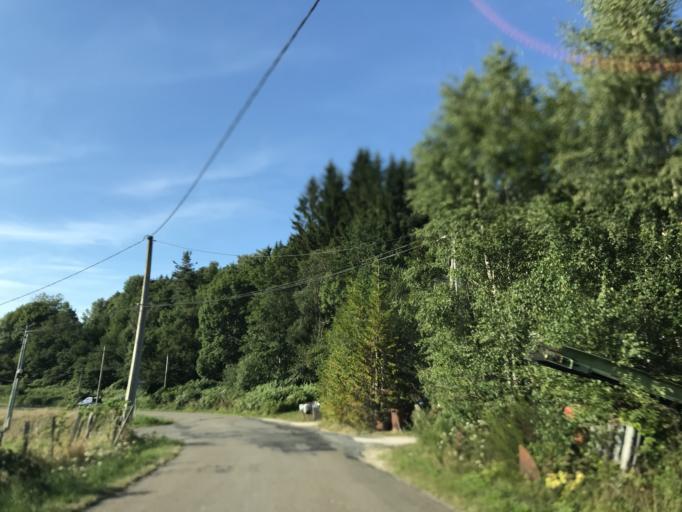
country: FR
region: Auvergne
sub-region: Departement du Puy-de-Dome
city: Job
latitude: 45.6912
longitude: 3.7316
